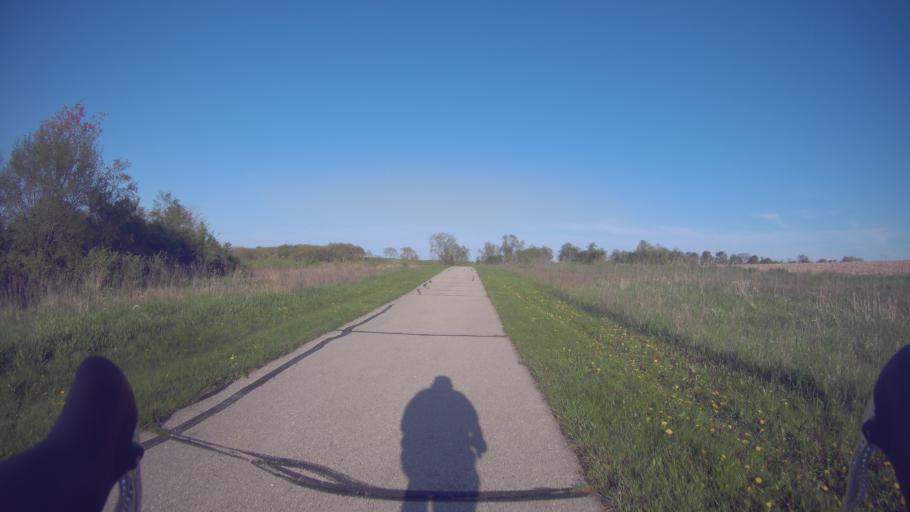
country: US
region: Wisconsin
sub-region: Dane County
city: Monona
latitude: 43.0229
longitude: -89.3589
